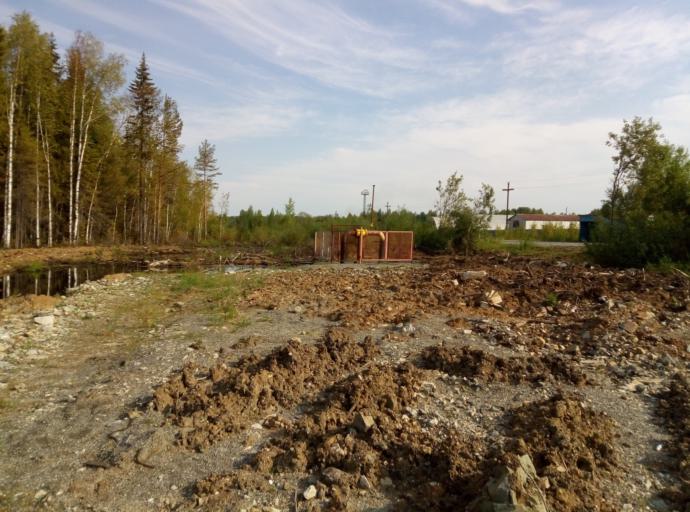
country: RU
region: Sverdlovsk
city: Krasnotur'insk
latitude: 59.7019
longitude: 60.2030
